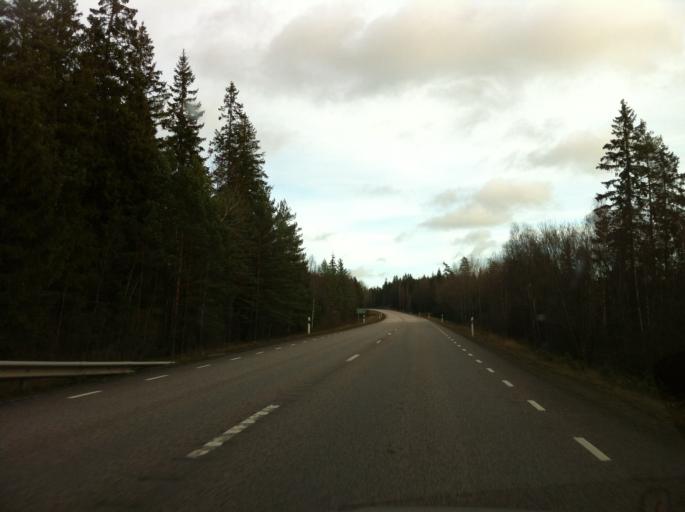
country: SE
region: Kronoberg
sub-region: Uppvidinge Kommun
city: Aseda
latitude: 57.1475
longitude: 15.2987
